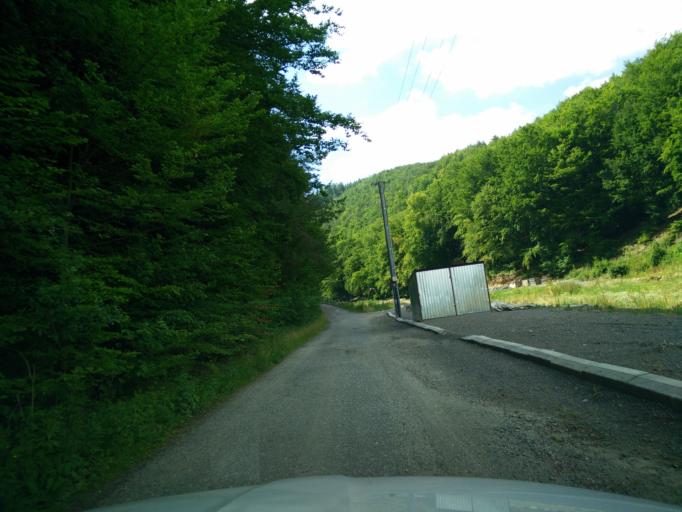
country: SK
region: Nitriansky
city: Bojnice
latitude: 48.8365
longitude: 18.5818
